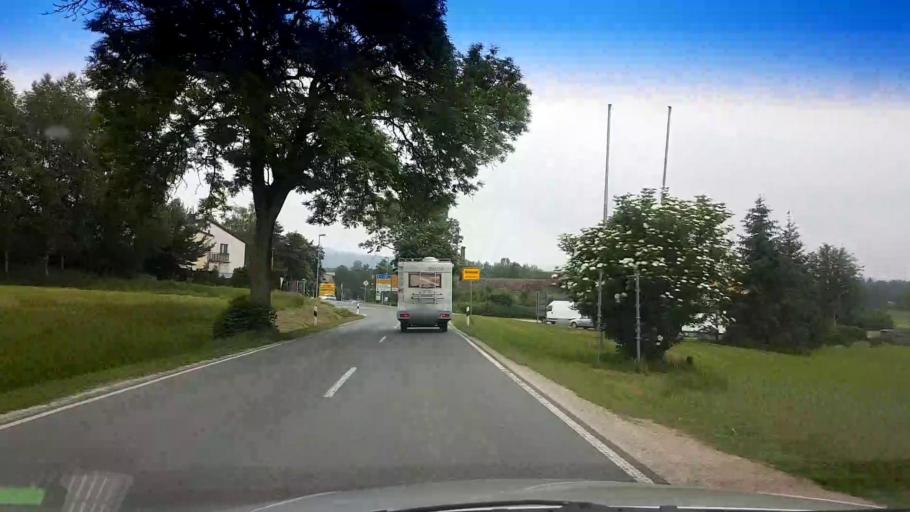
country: DE
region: Bavaria
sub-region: Upper Franconia
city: Weissenstadt
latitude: 50.0960
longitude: 11.8921
